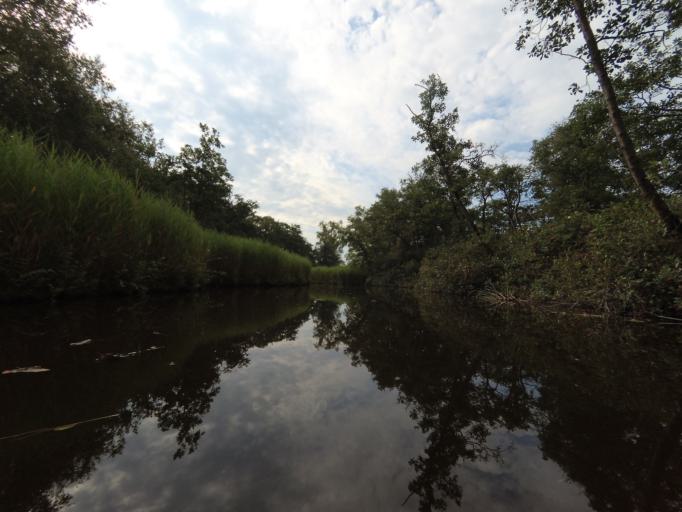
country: NL
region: South Holland
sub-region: Gemeente Nieuwkoop
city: Nieuwkoop
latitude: 52.1539
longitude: 4.8246
